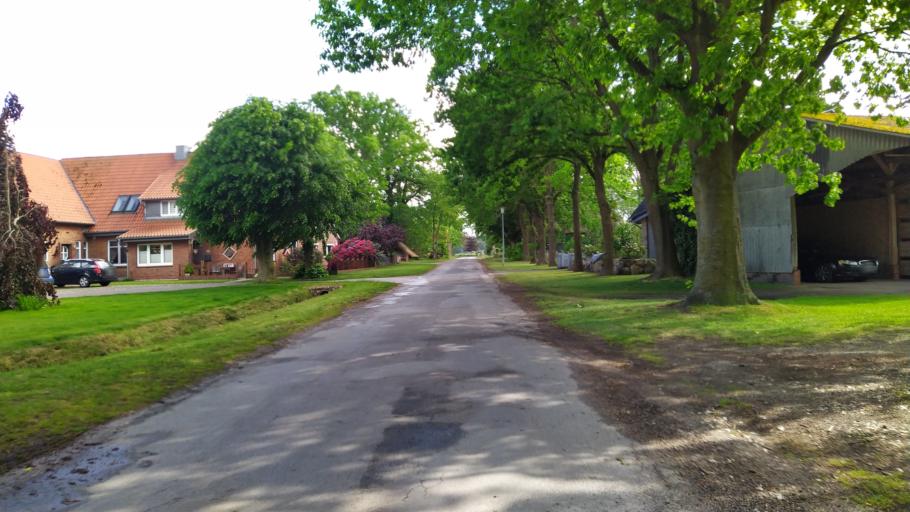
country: DE
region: Lower Saxony
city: Brest
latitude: 53.4508
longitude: 9.3867
